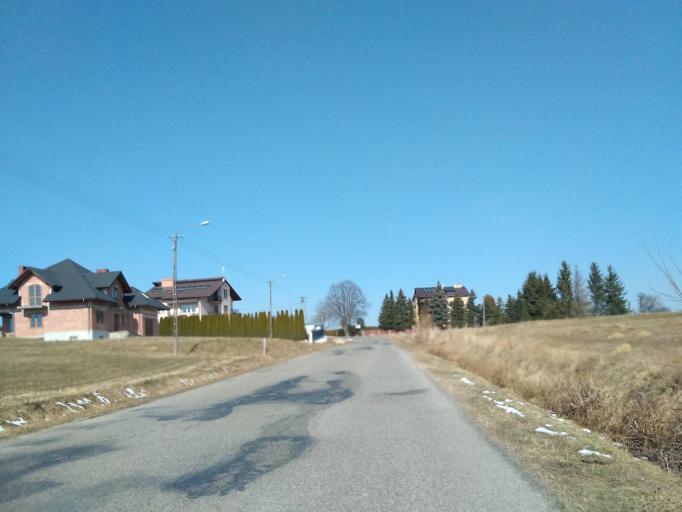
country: PL
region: Subcarpathian Voivodeship
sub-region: Powiat brzozowski
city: Jasienica Rosielna
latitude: 49.7646
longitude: 21.9272
